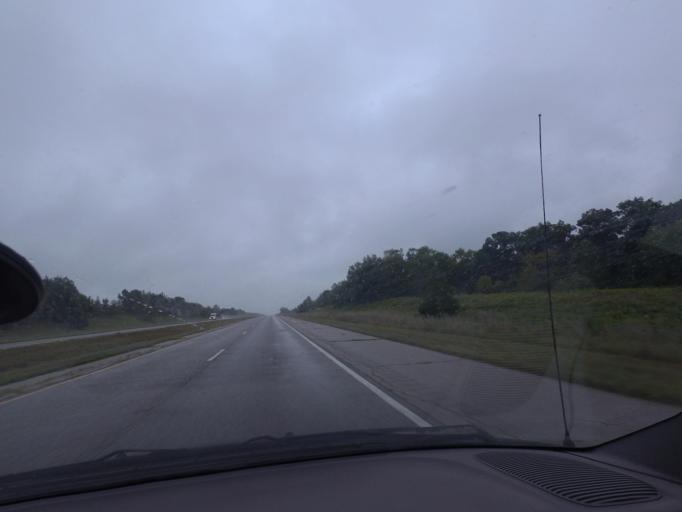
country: US
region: Illinois
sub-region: Pike County
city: Barry
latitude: 39.6916
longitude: -90.9360
